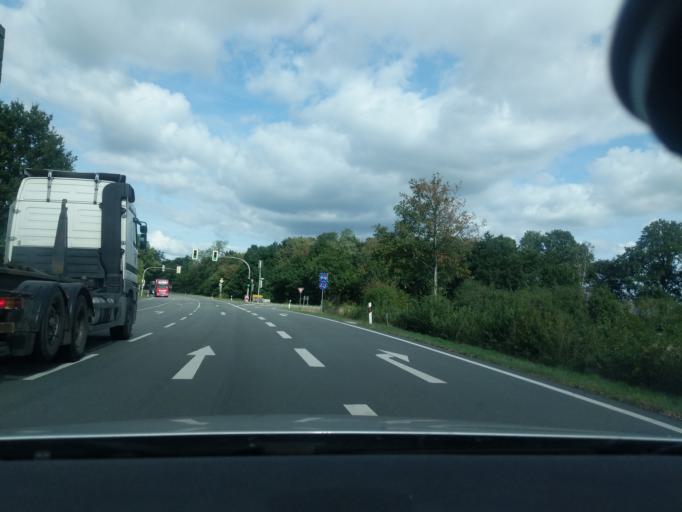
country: DE
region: Lower Saxony
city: Bohmte
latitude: 52.3798
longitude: 8.3106
